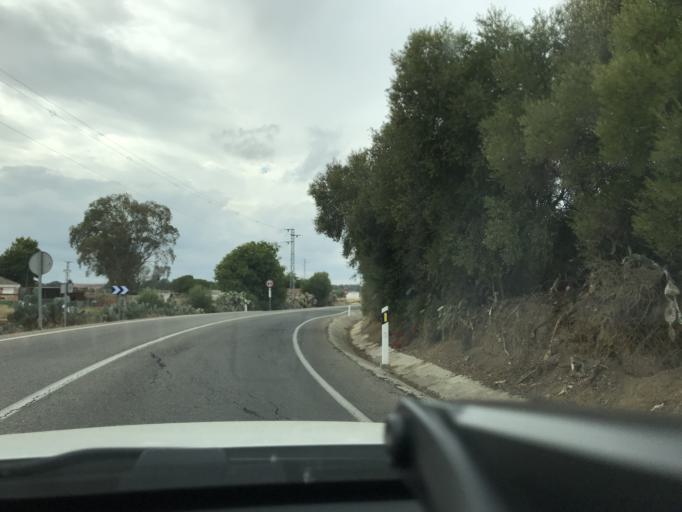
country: ES
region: Andalusia
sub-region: Provincia de Sevilla
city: Villanueva del Rio y Minas
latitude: 37.6355
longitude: -5.7293
